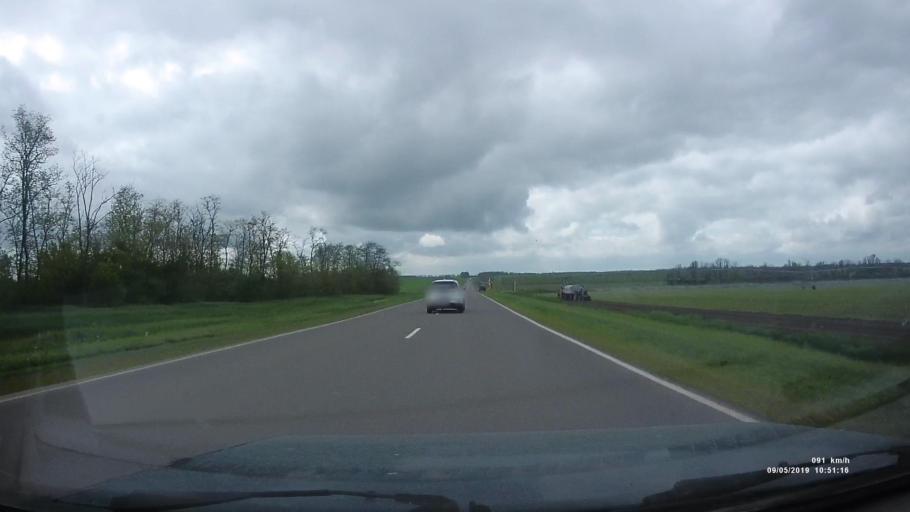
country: RU
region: Rostov
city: Peshkovo
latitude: 46.9172
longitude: 39.3552
